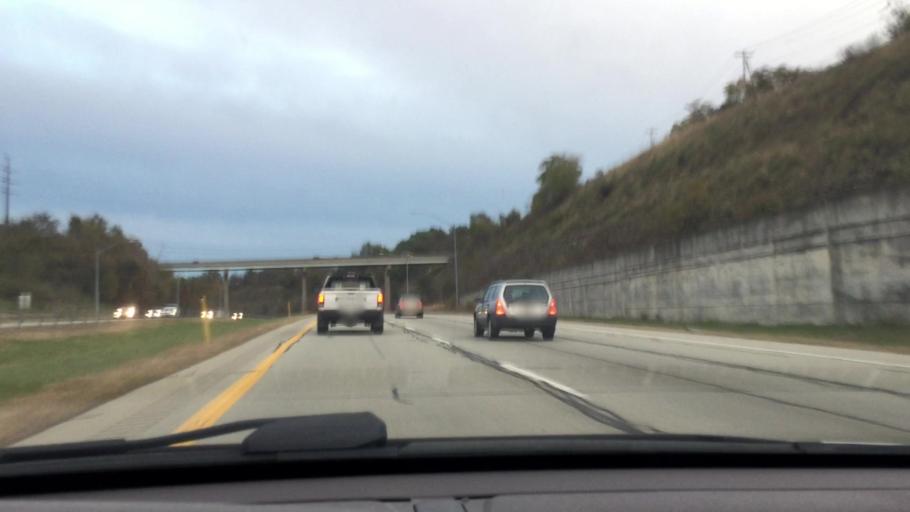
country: US
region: Pennsylvania
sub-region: Westmoreland County
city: Arnold
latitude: 40.5702
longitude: -79.7939
